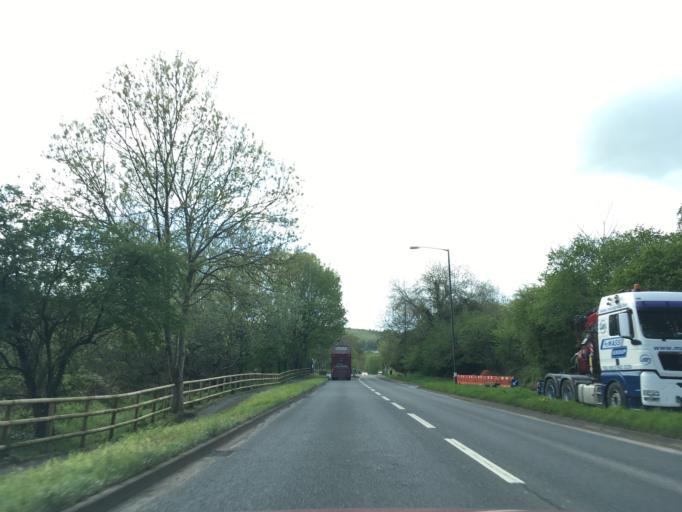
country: GB
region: England
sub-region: Gloucestershire
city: Brimscombe
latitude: 51.7235
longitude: -2.1974
